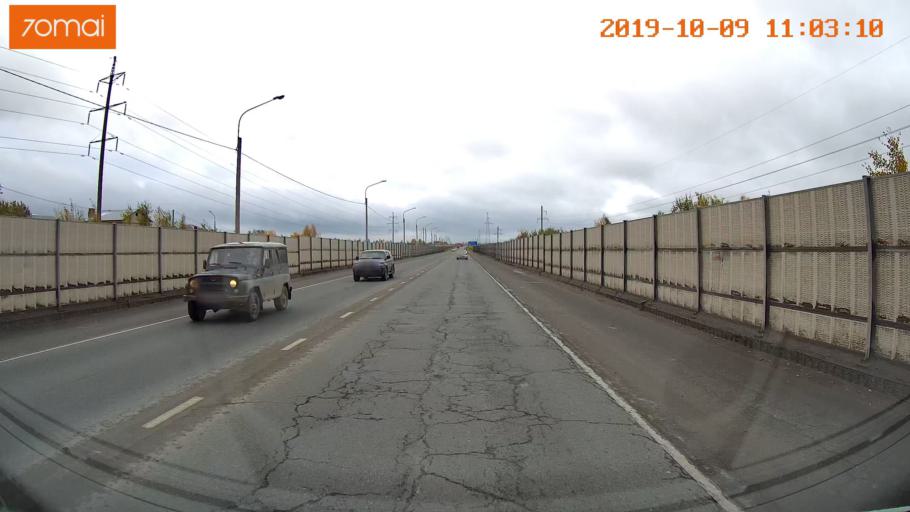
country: RU
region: Vologda
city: Vologda
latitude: 59.2219
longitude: 39.7767
